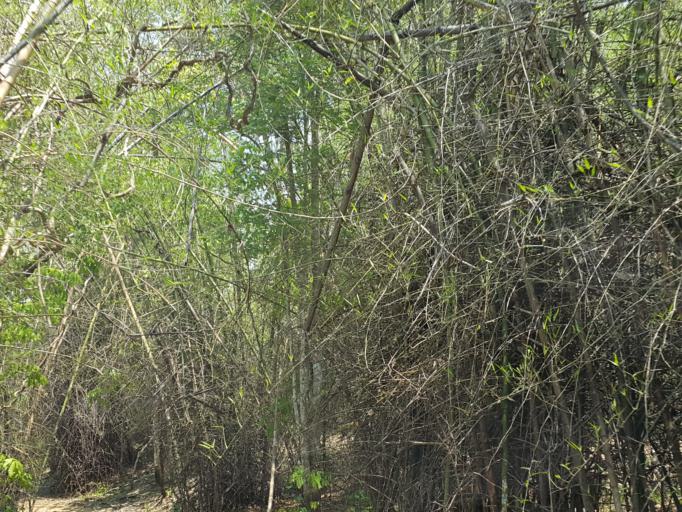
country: TH
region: Kanchanaburi
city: Sai Yok
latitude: 14.2108
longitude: 98.8809
